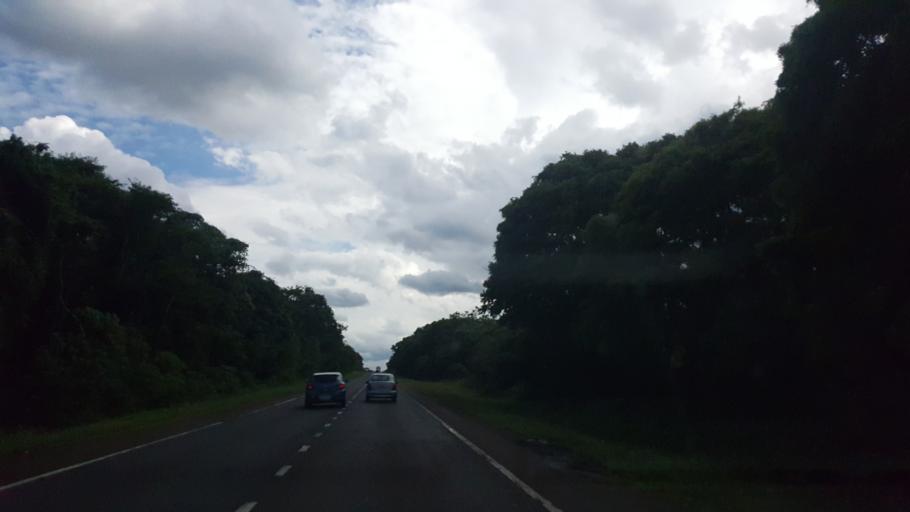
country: AR
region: Misiones
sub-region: Departamento de Iguazu
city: Puerto Iguazu
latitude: -25.7095
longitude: -54.5173
